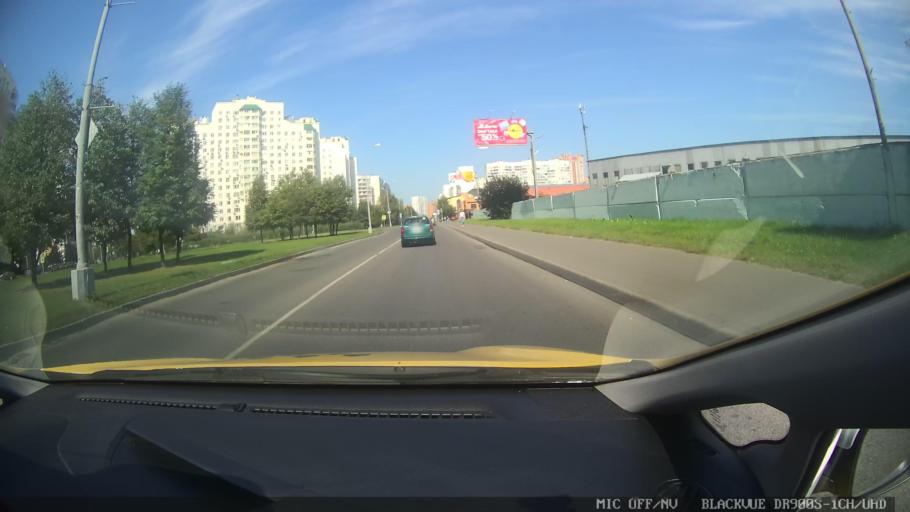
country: RU
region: Moscow
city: Zhulebino
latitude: 55.6779
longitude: 37.8592
